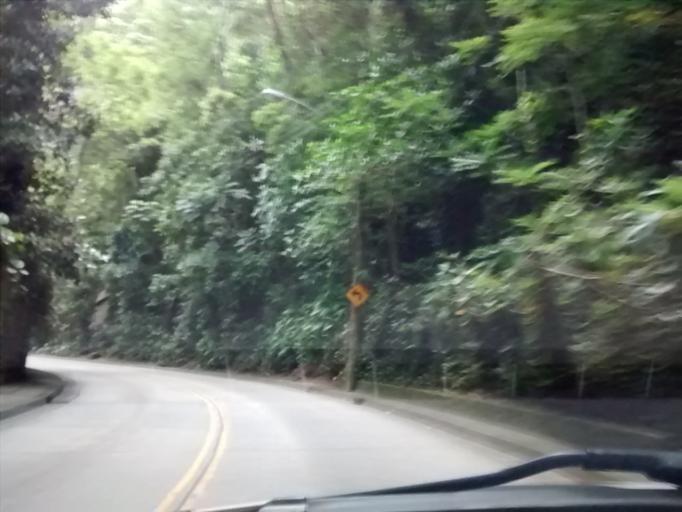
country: BR
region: Rio de Janeiro
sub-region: Rio De Janeiro
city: Rio de Janeiro
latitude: -22.9832
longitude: -43.2766
